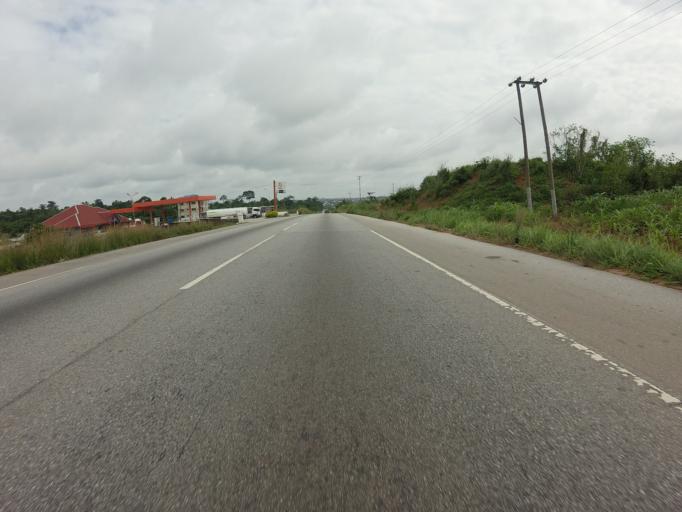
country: GH
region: Ashanti
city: Tafo
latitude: 7.0015
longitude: -1.7007
